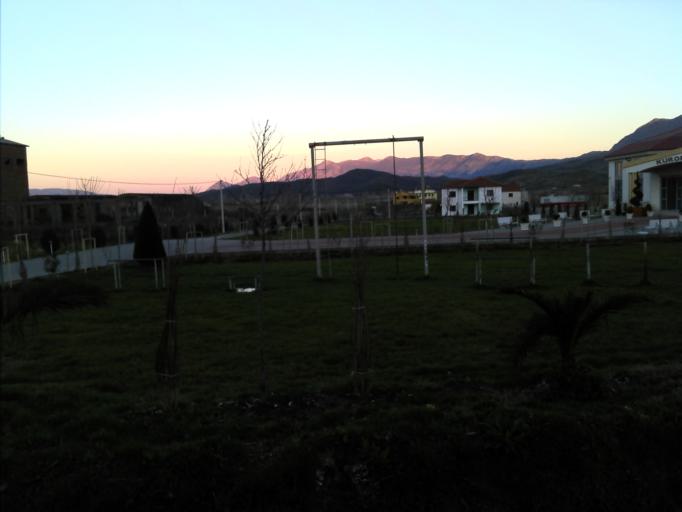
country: AL
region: Shkoder
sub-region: Rrethi i Shkodres
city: Berdica e Madhe
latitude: 42.0174
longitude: 19.4847
